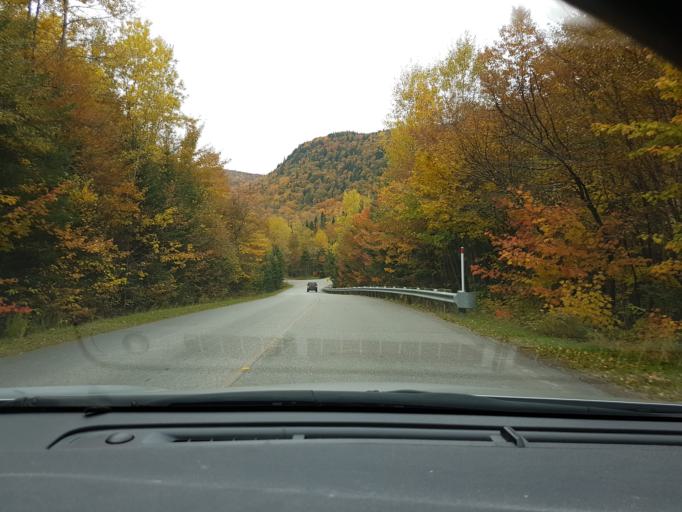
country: CA
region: Quebec
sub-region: Capitale-Nationale
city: Shannon
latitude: 47.1093
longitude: -71.3638
